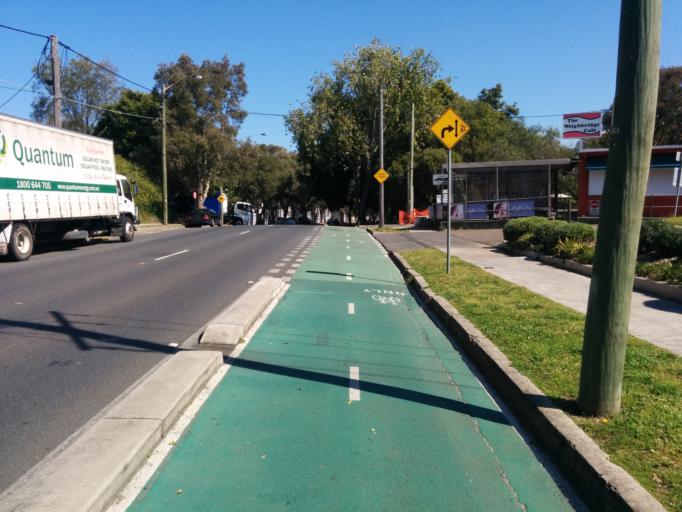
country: AU
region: New South Wales
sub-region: City of Sydney
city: Alexandria
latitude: -33.9078
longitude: 151.1975
